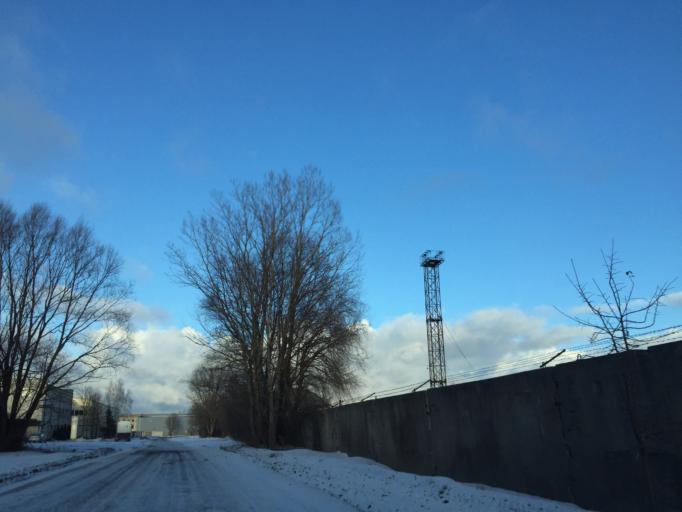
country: LV
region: Riga
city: Riga
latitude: 56.9866
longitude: 24.1113
